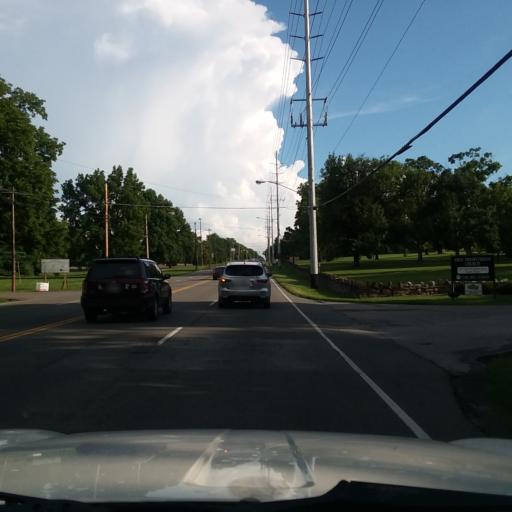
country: US
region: Tennessee
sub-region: Davidson County
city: Oak Hill
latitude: 36.0805
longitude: -86.7728
